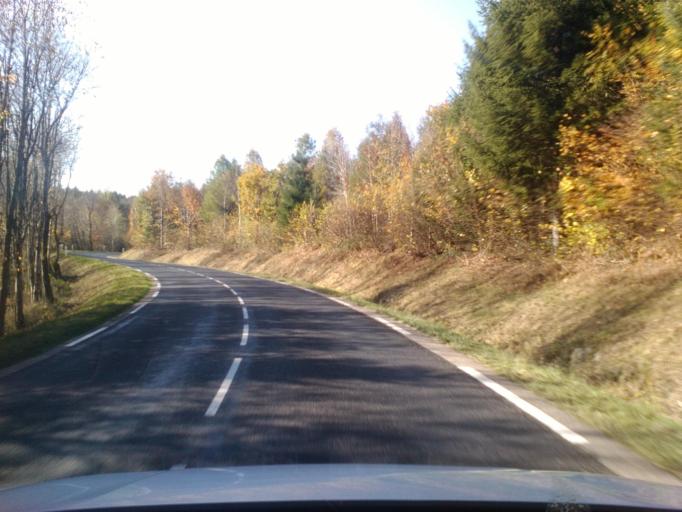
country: FR
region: Lorraine
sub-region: Departement des Vosges
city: Senones
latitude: 48.4017
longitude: 7.0114
